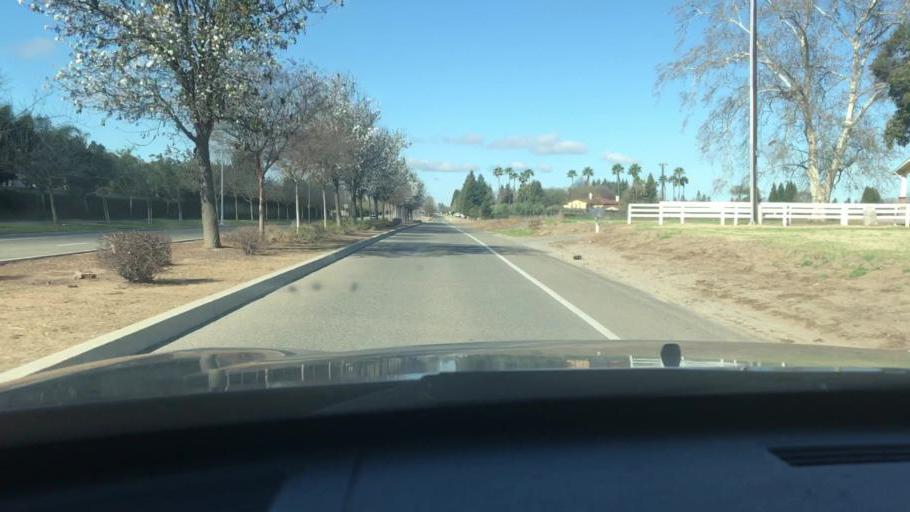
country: US
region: California
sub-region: Fresno County
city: Clovis
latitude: 36.8665
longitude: -119.6724
